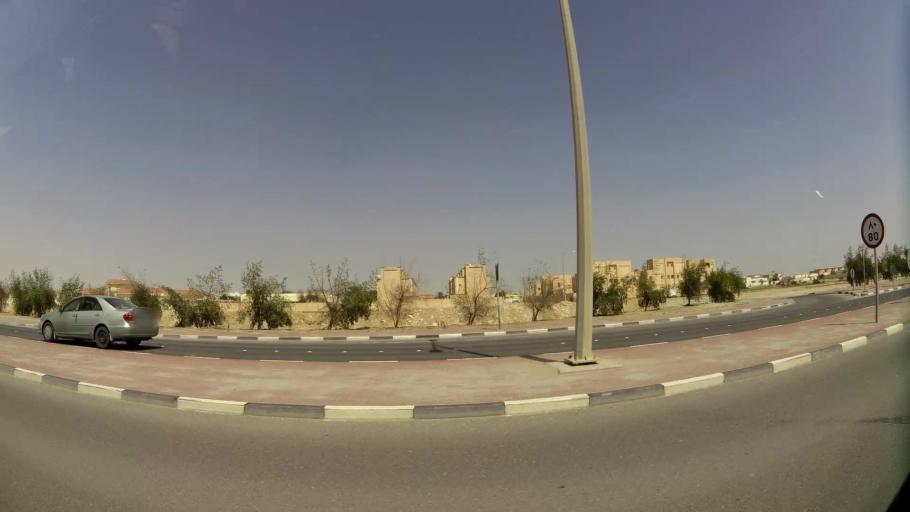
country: QA
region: Baladiyat Umm Salal
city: Umm Salal Muhammad
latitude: 25.3903
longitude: 51.4214
